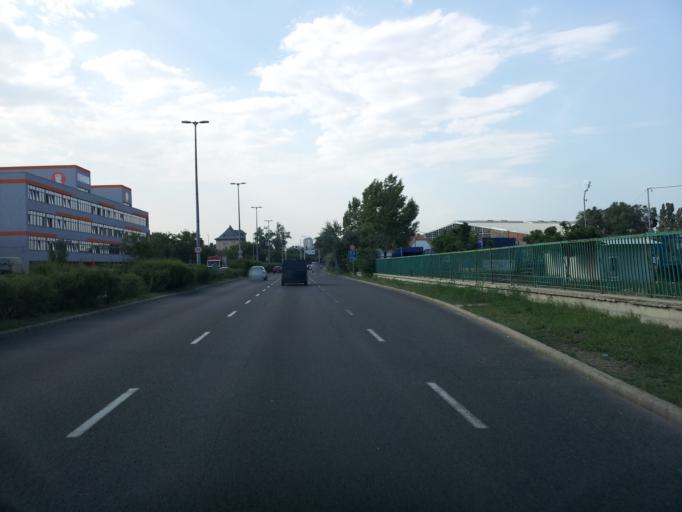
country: HU
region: Budapest
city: Budapest XX. keruelet
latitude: 47.4641
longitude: 19.1061
